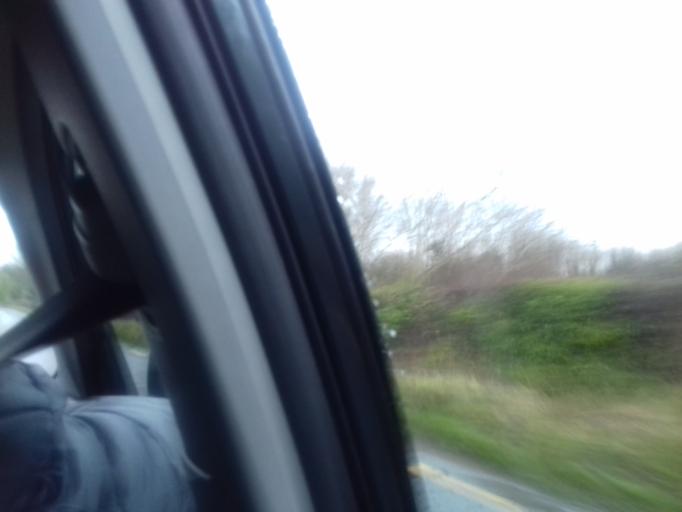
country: IE
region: Leinster
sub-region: Kilkenny
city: Graiguenamanagh
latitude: 52.5919
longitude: -6.9696
